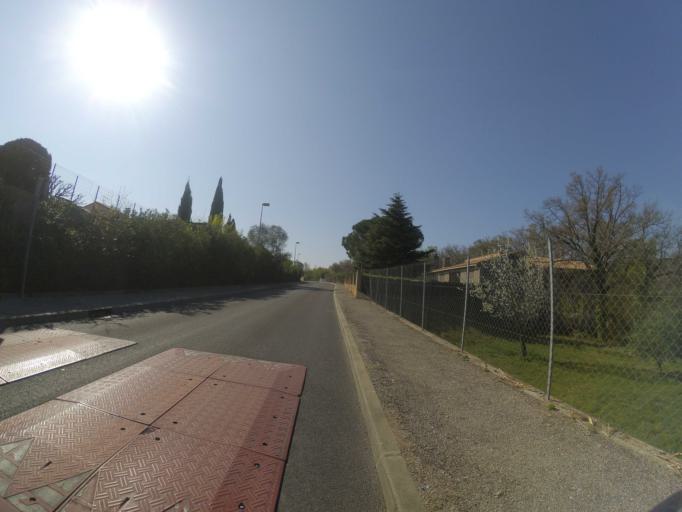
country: FR
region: Languedoc-Roussillon
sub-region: Departement des Pyrenees-Orientales
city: Thuir
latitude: 42.6239
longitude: 2.7507
